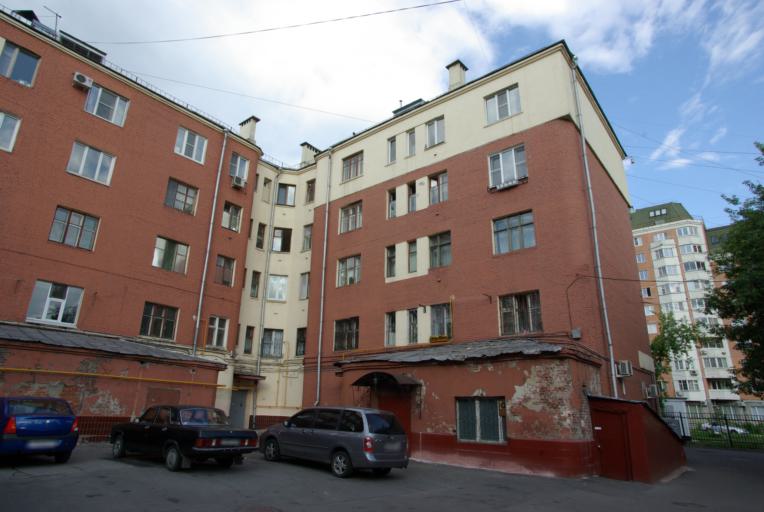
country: RU
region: Moscow
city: Lefortovo
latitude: 55.7736
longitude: 37.6926
